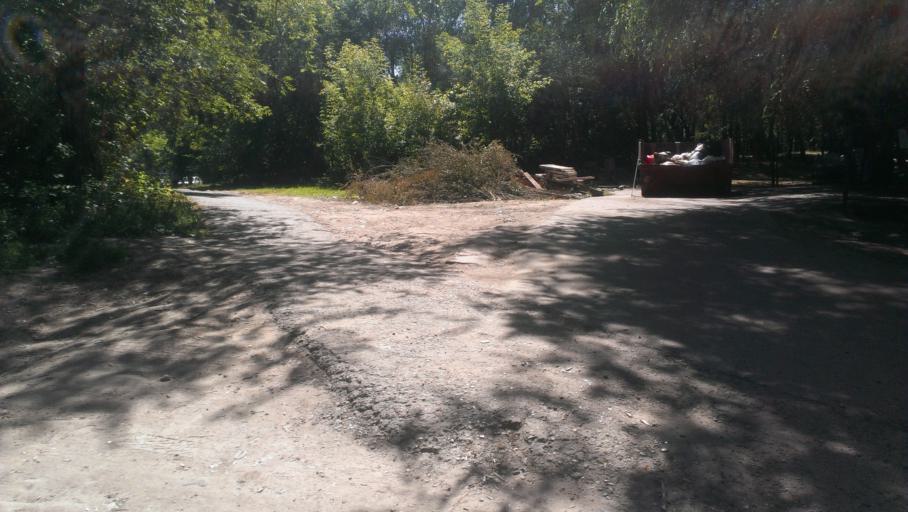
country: RU
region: Altai Krai
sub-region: Gorod Barnaulskiy
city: Barnaul
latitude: 53.3628
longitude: 83.6933
